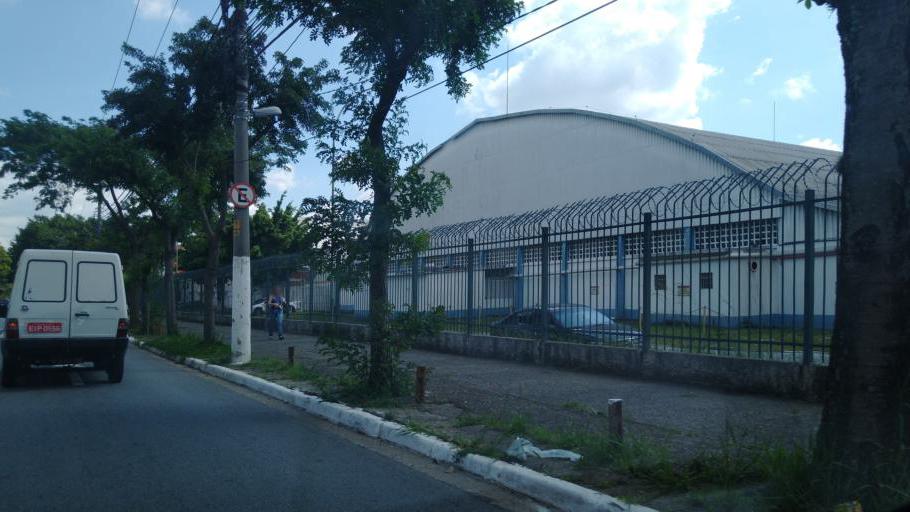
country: BR
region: Sao Paulo
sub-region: Sao Paulo
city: Sao Paulo
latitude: -23.5142
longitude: -46.6365
